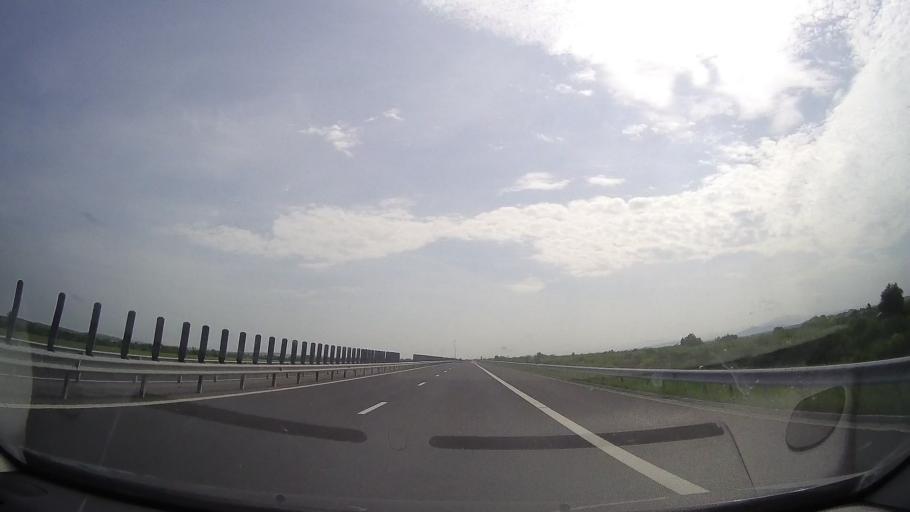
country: RO
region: Timis
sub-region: Comuna Bethausen
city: Bethausen
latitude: 45.8054
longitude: 21.9076
